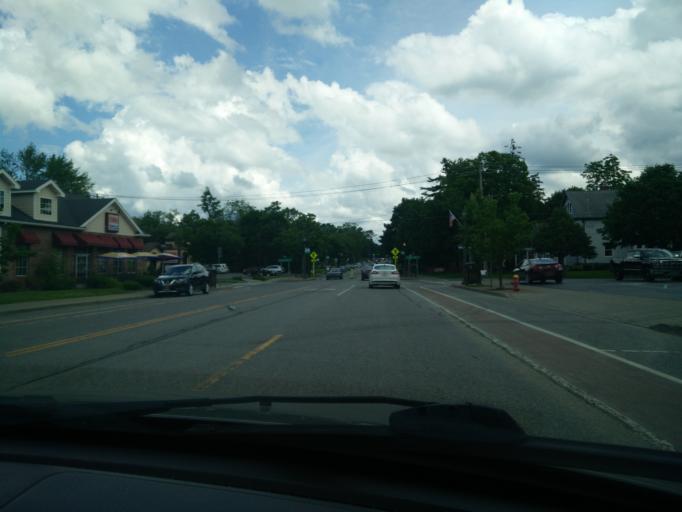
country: US
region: New York
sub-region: Erie County
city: East Aurora
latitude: 42.7679
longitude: -78.6265
